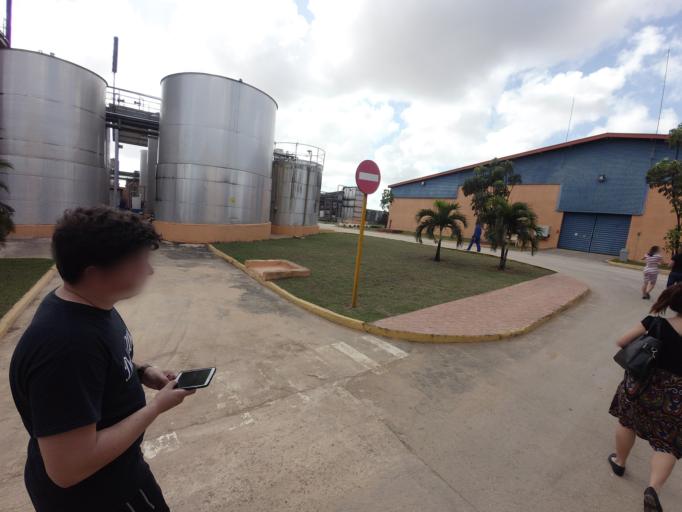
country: CU
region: Mayabeque
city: San Jose de las Lajas
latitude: 22.9309
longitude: -82.1025
